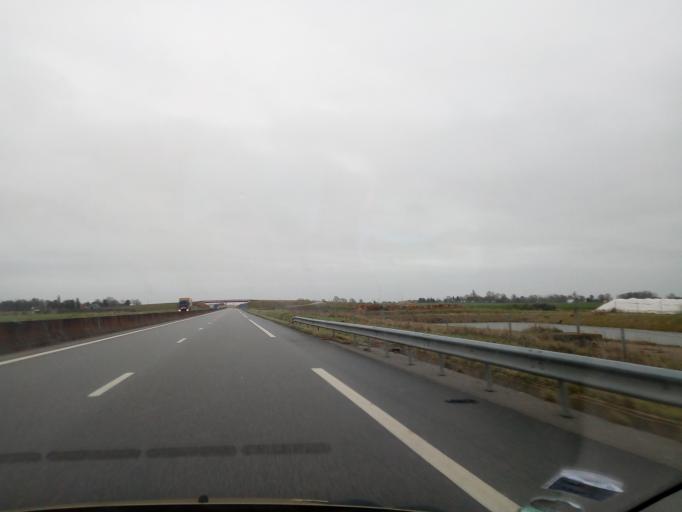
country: FR
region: Haute-Normandie
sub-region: Departement de l'Eure
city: Menneval
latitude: 49.1435
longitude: 0.5898
